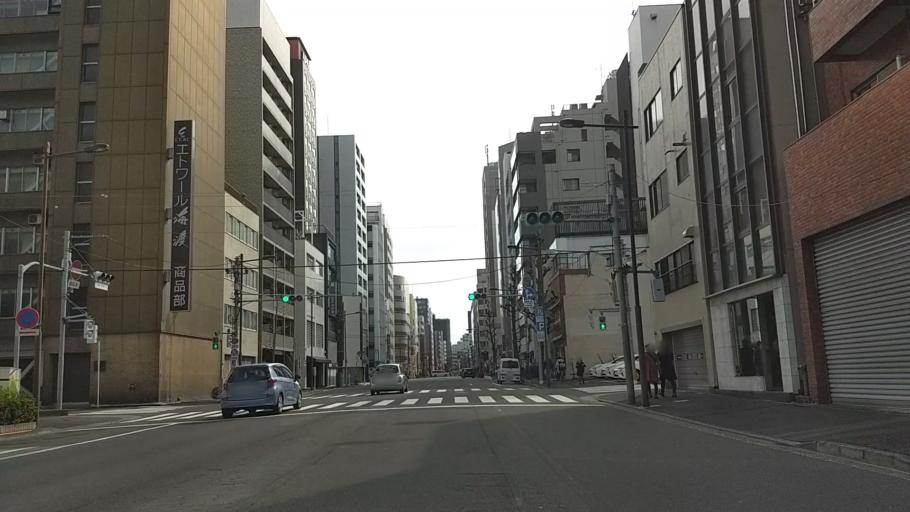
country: JP
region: Tokyo
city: Tokyo
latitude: 35.6943
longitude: 139.7803
